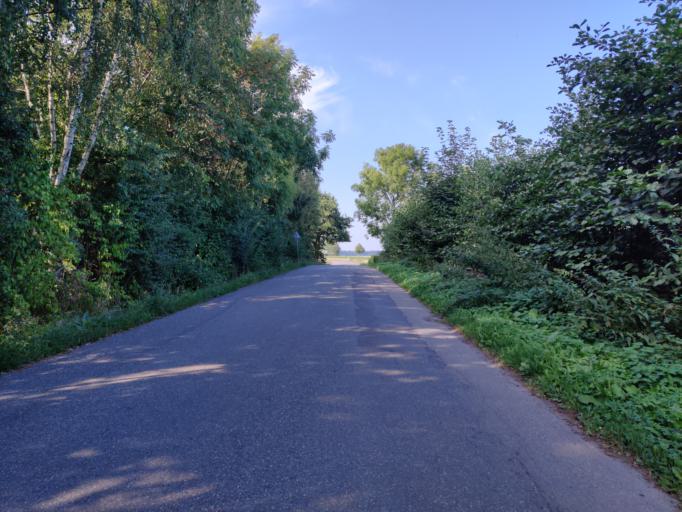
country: DK
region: Zealand
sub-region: Guldborgsund Kommune
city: Nykobing Falster
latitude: 54.7209
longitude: 11.9270
